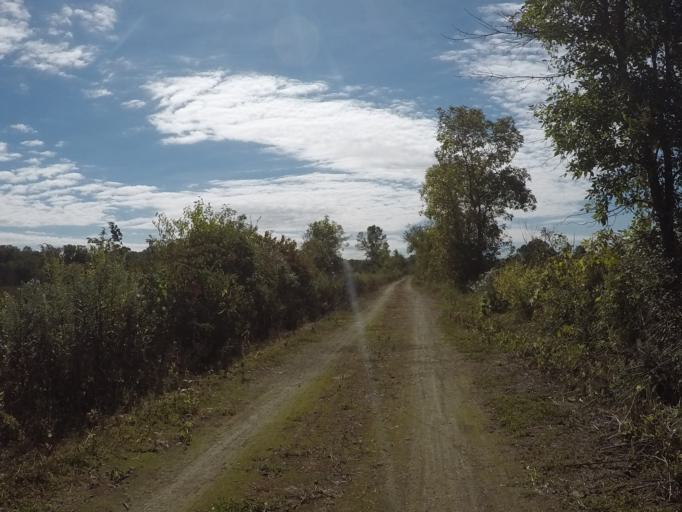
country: US
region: Wisconsin
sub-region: Richland County
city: Richland Center
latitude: 43.2726
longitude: -90.3103
